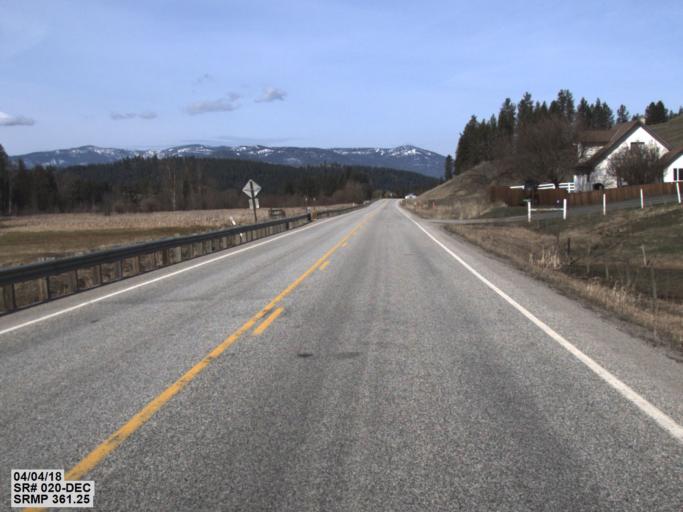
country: US
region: Washington
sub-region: Stevens County
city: Colville
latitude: 48.5149
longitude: -117.7827
